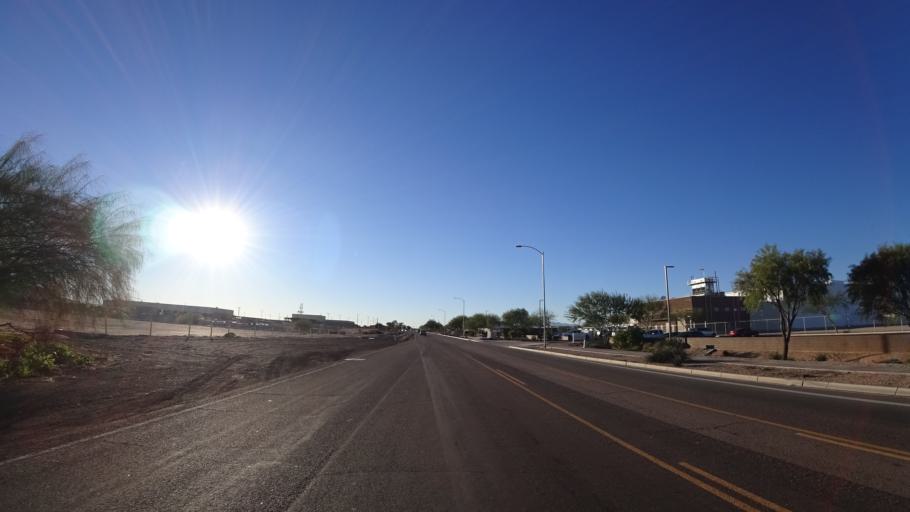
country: US
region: Arizona
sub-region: Maricopa County
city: Tolleson
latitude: 33.4517
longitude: -112.2233
